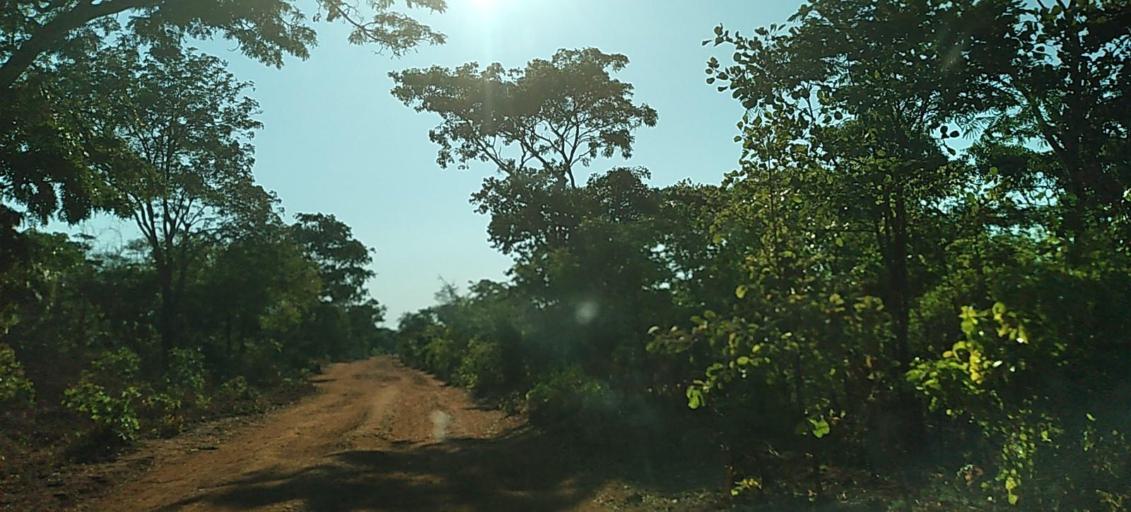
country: ZM
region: Copperbelt
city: Luanshya
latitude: -13.4592
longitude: 28.8117
